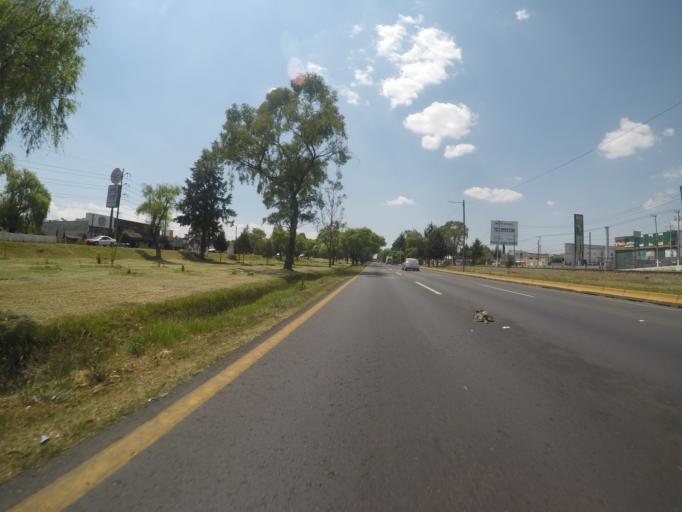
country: MX
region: Mexico
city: Santa Maria Totoltepec
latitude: 19.2870
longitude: -99.5785
